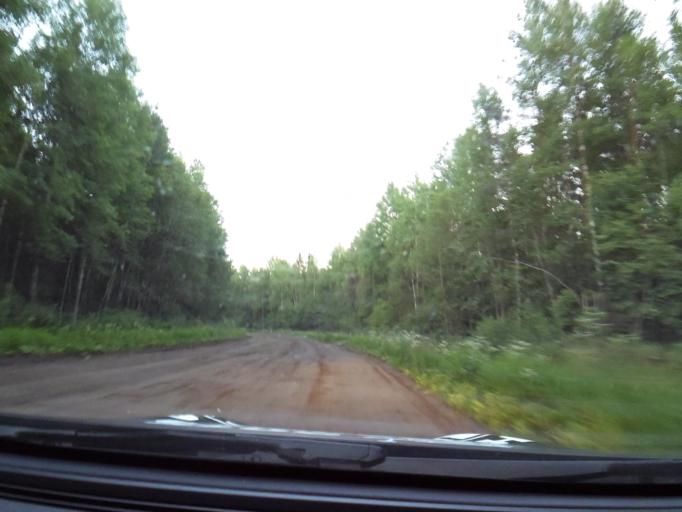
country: RU
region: Leningrad
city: Voznesen'ye
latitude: 60.8547
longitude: 35.8772
